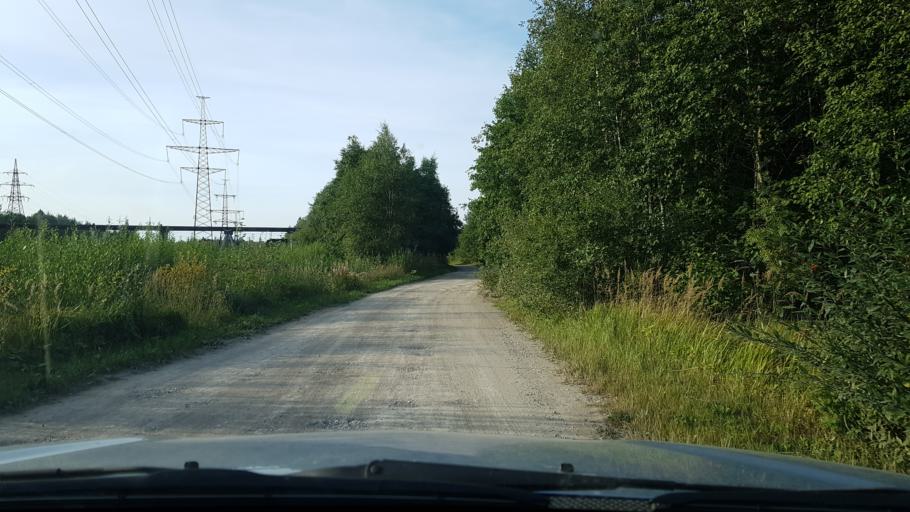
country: EE
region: Ida-Virumaa
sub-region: Sillamaee linn
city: Sillamae
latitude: 59.2759
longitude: 27.9203
